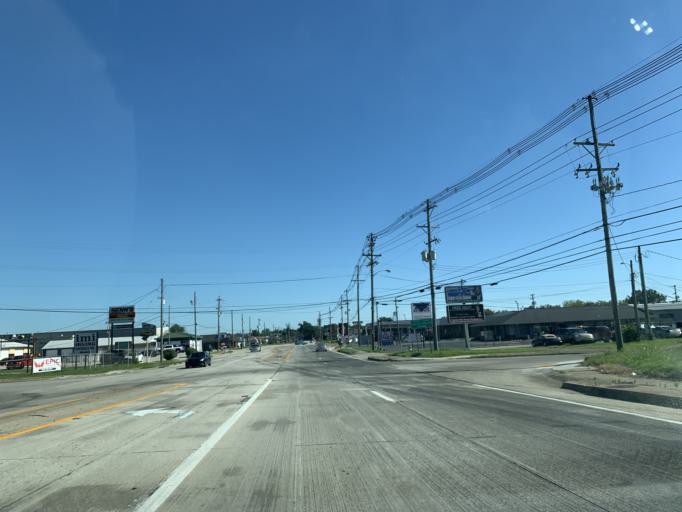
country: US
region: Kentucky
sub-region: Jefferson County
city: Audubon Park
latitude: 38.1888
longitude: -85.7030
